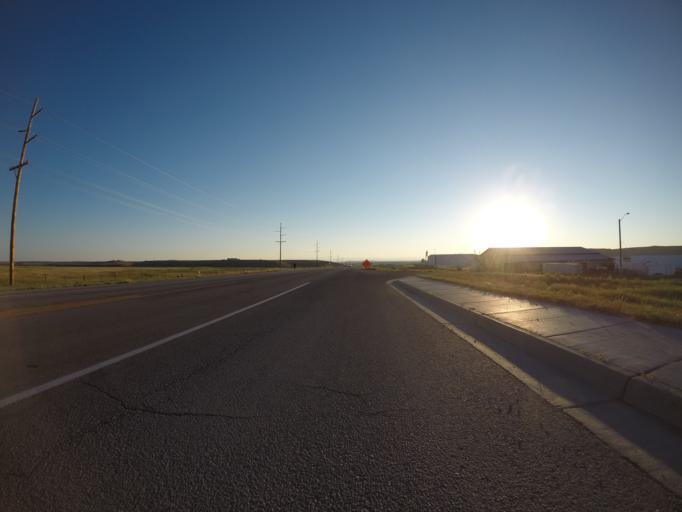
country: US
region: Wyoming
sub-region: Sublette County
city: Marbleton
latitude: 42.5612
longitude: -110.1050
